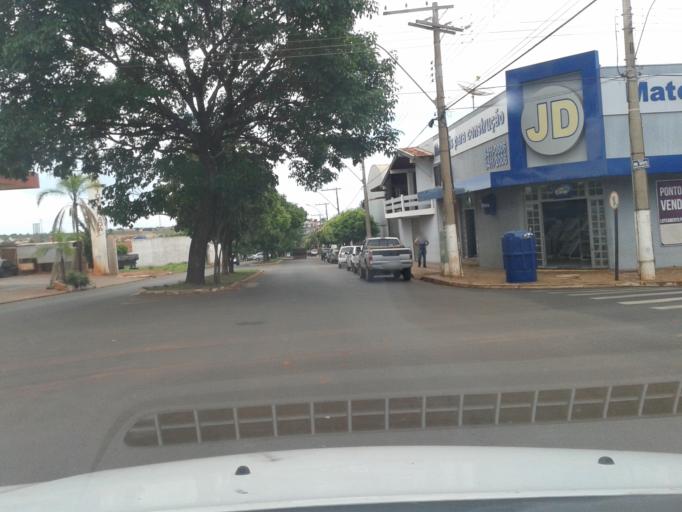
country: BR
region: Minas Gerais
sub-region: Iturama
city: Iturama
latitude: -19.7314
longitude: -50.1932
